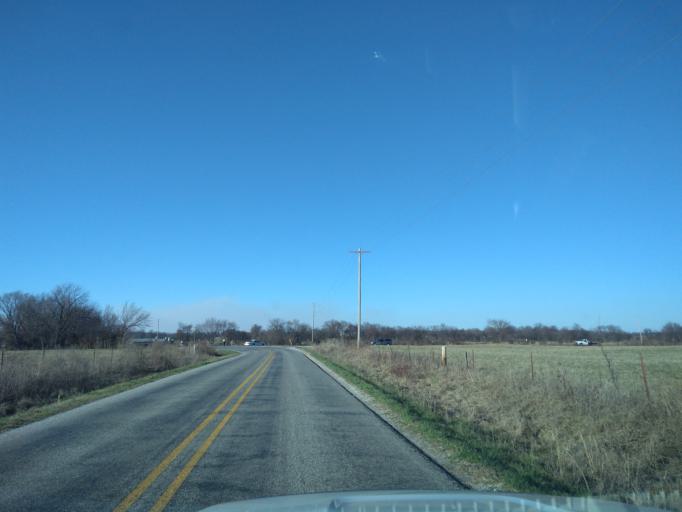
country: US
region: Arkansas
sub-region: Washington County
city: Lincoln
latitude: 36.0149
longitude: -94.3924
